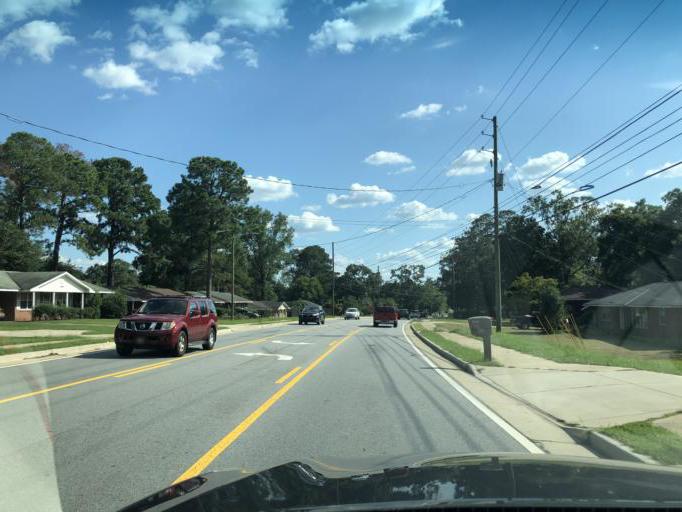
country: US
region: Georgia
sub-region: Muscogee County
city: Columbus
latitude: 32.5369
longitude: -84.9239
